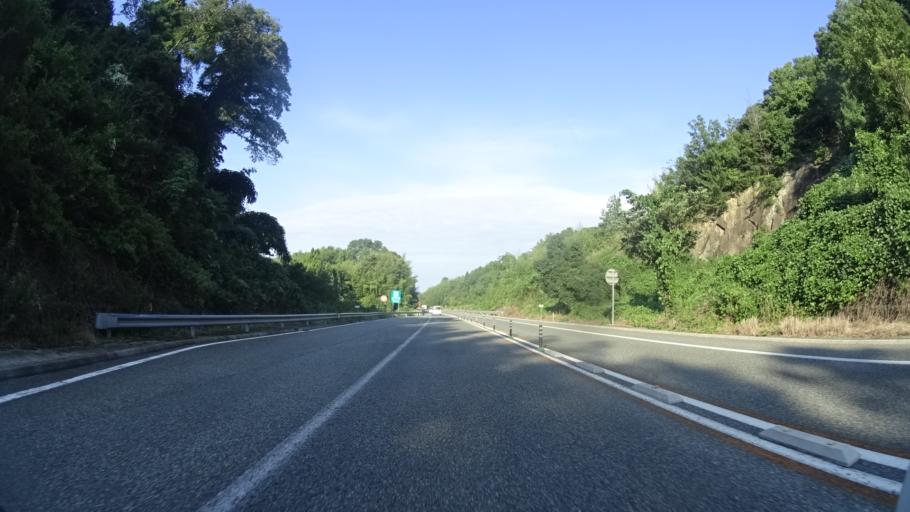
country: JP
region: Shimane
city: Matsue-shi
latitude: 35.4120
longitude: 132.9545
